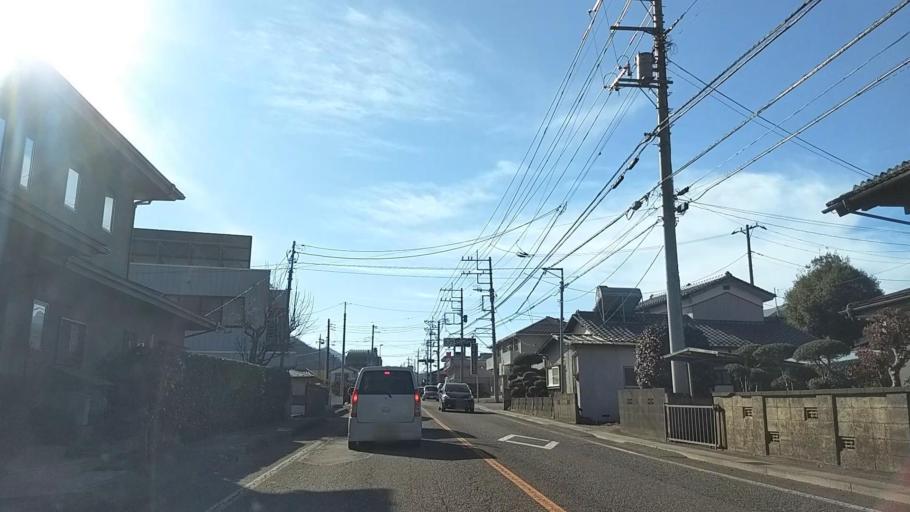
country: JP
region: Yamanashi
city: Otsuki
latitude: 35.5773
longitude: 138.9331
